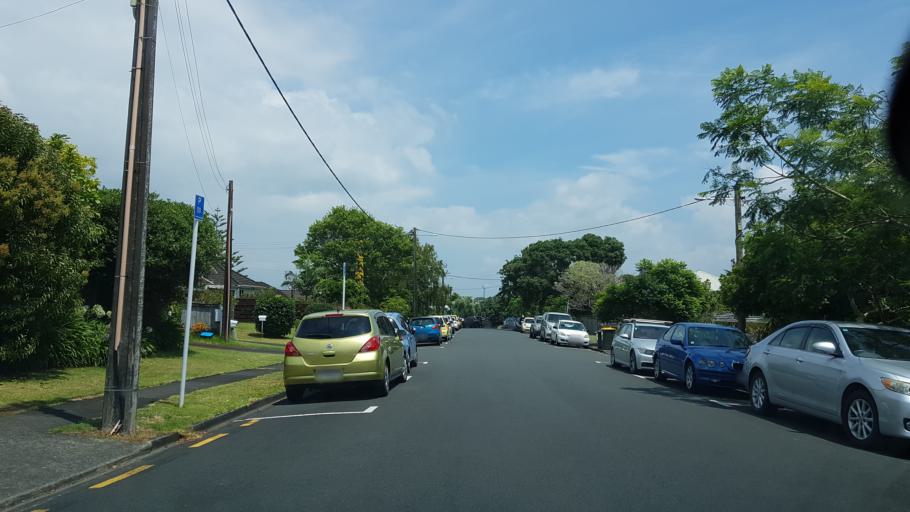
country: NZ
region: Auckland
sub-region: Auckland
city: North Shore
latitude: -36.7920
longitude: 174.7692
